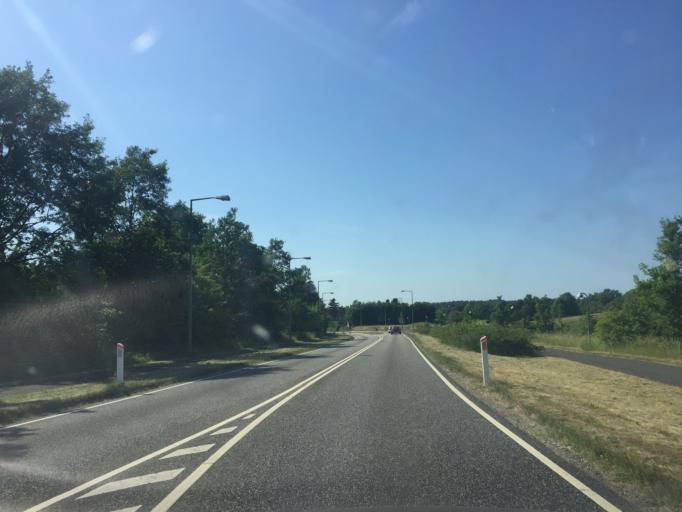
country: DK
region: Capital Region
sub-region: Ballerup Kommune
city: Malov
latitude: 55.7864
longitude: 12.3243
